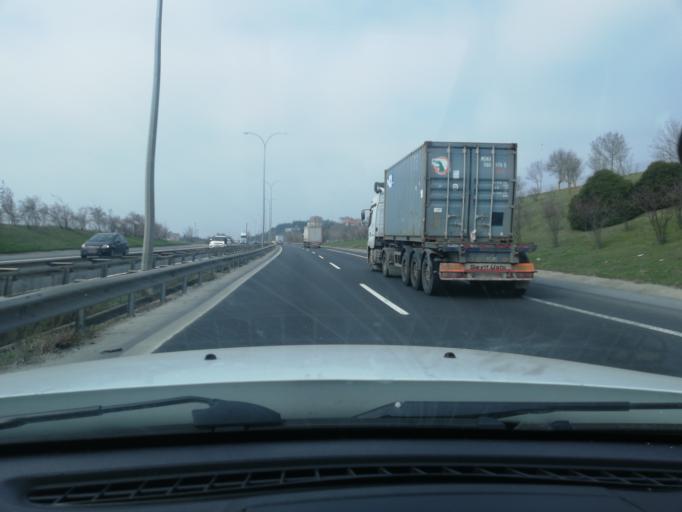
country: TR
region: Istanbul
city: Celaliye
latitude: 41.0555
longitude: 28.4257
